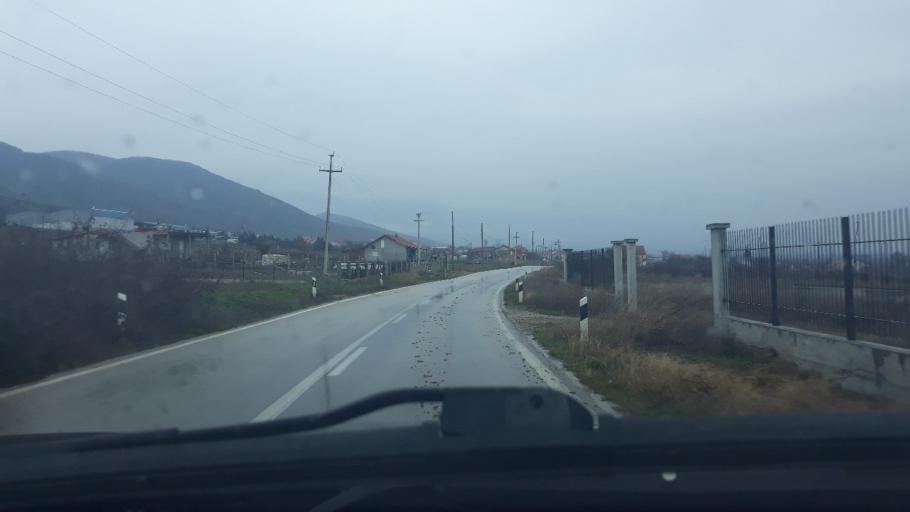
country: MK
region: Dojran
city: Star Dojran
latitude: 41.2575
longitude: 22.7374
